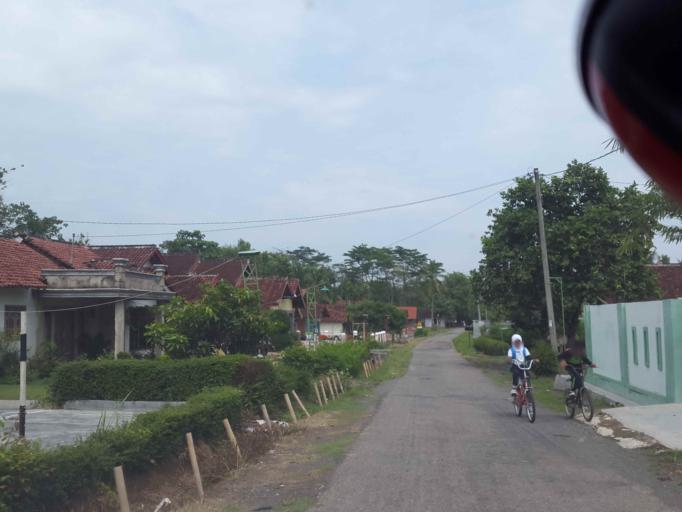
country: ID
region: Lampung
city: Natar
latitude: -5.2537
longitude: 105.1968
